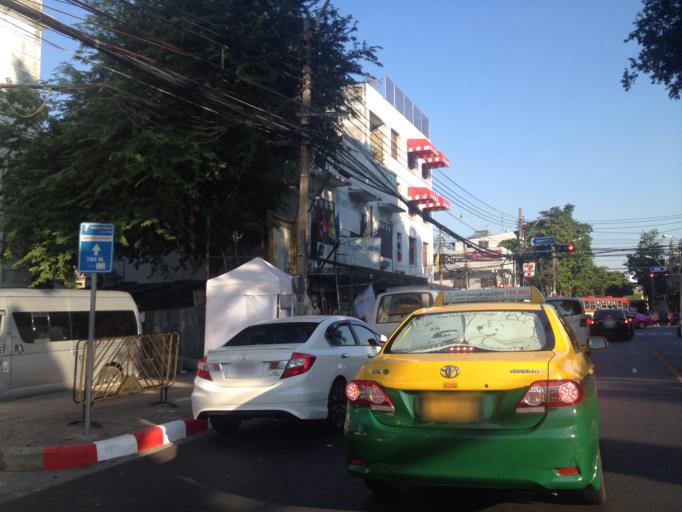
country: TH
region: Bangkok
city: Bangkok
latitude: 13.7597
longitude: 100.5020
